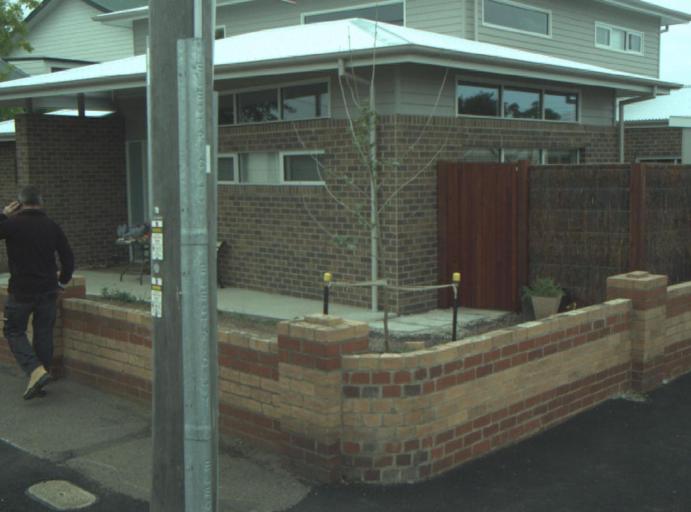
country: AU
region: Victoria
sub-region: Greater Geelong
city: Geelong West
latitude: -38.1241
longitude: 144.3569
